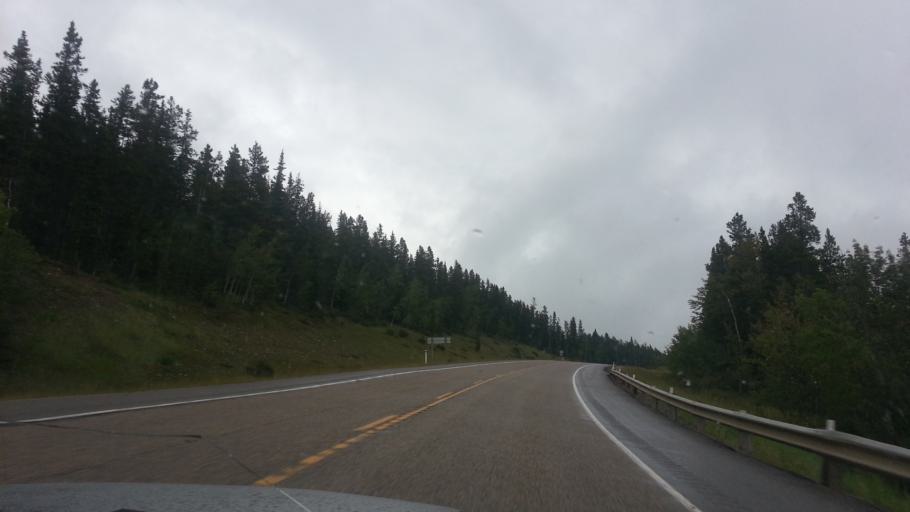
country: CA
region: Alberta
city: Cochrane
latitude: 50.8689
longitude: -114.7805
